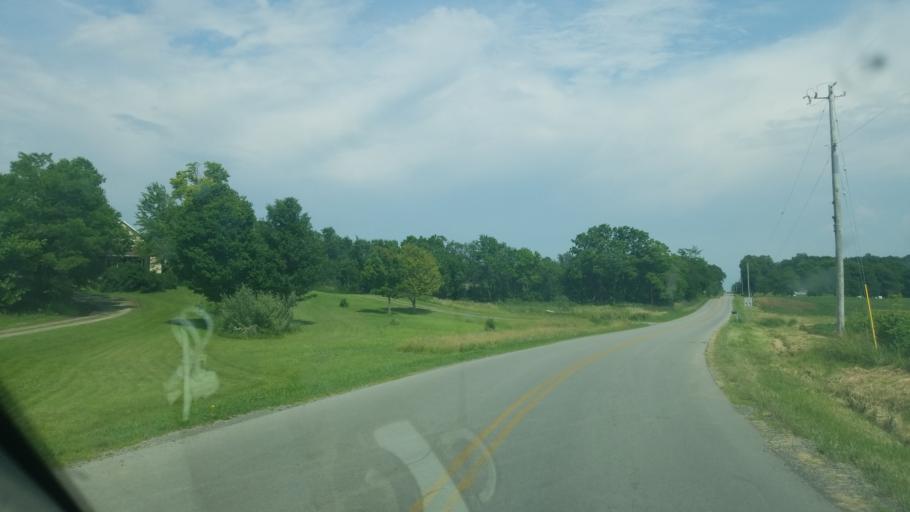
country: US
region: Ohio
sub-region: Logan County
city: West Liberty
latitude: 40.3007
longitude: -83.6554
